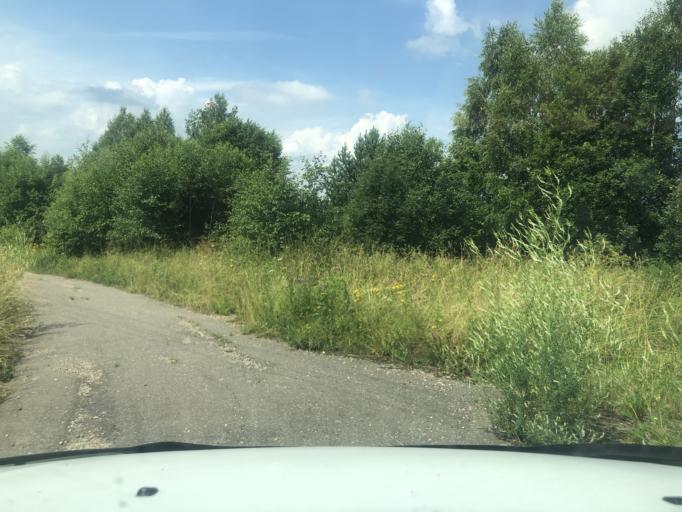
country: RU
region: Jaroslavl
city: Pereslavl'-Zalesskiy
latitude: 57.0456
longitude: 38.8732
